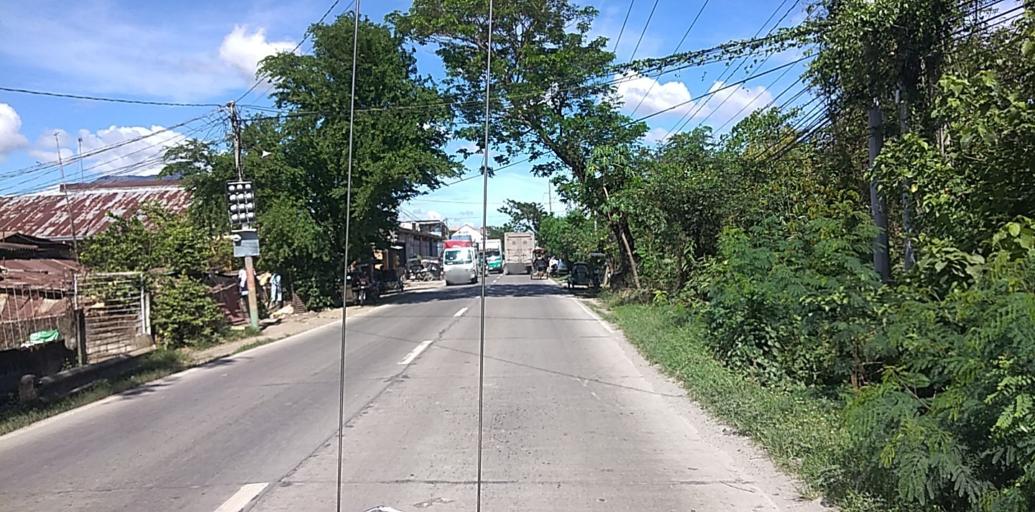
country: PH
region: Central Luzon
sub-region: Province of Pampanga
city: Arayat
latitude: 15.1234
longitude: 120.7758
